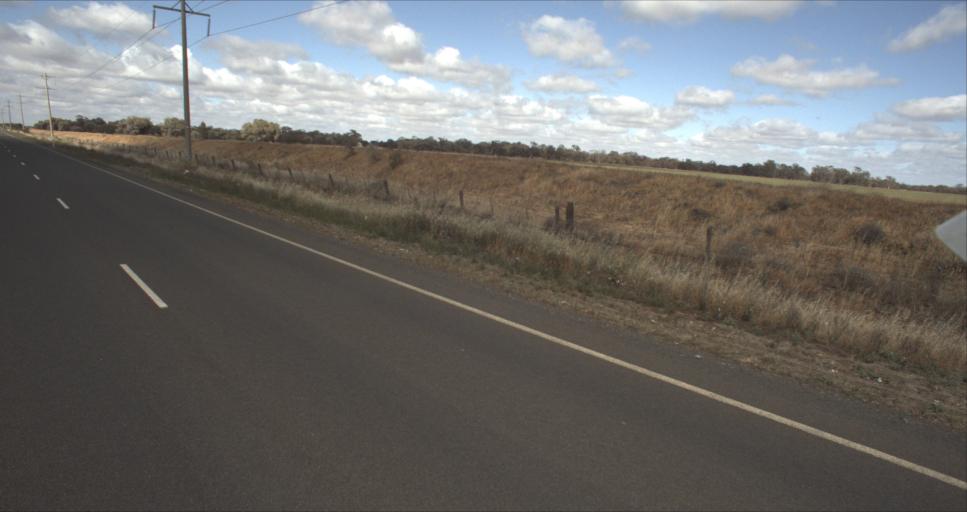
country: AU
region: New South Wales
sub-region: Murrumbidgee Shire
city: Darlington Point
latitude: -34.5373
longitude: 146.1728
